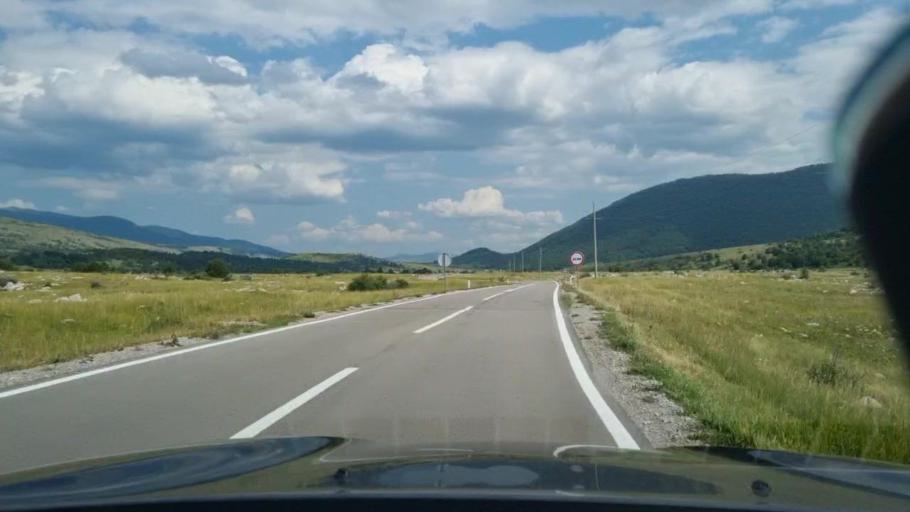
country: BA
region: Federation of Bosnia and Herzegovina
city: Bosansko Grahovo
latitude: 44.1451
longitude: 16.4603
